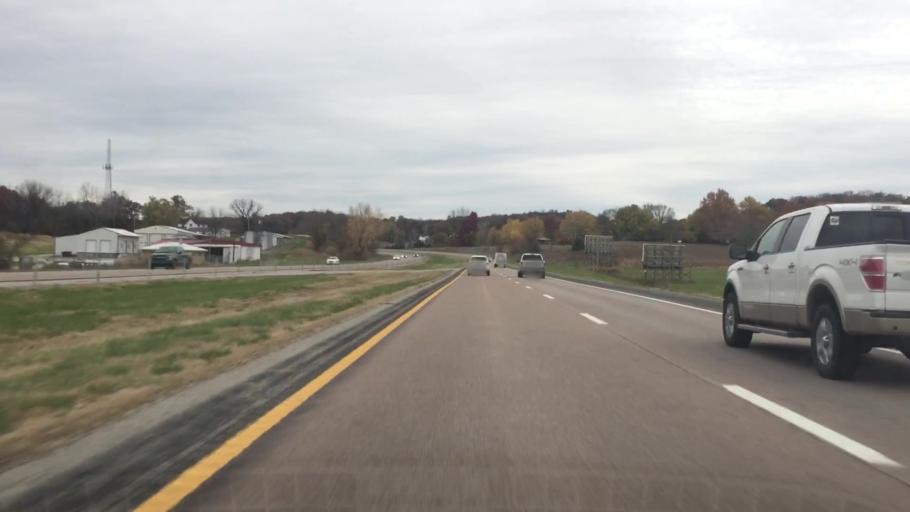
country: US
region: Missouri
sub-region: Cole County
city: Jefferson City
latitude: 38.6464
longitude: -92.2020
